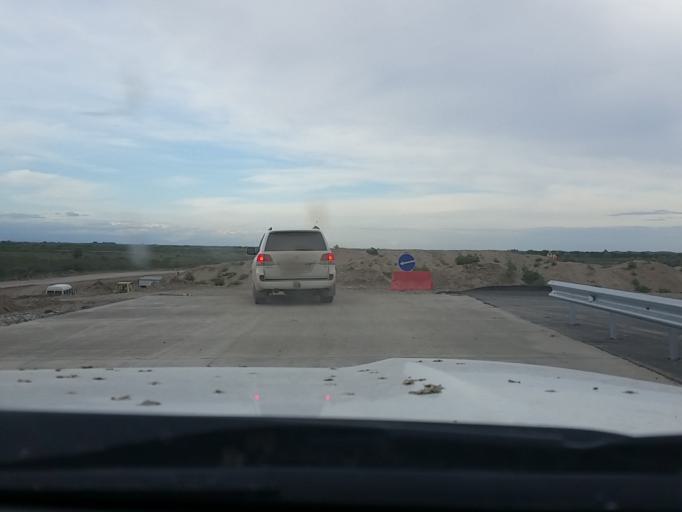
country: KZ
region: Almaty Oblysy
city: Zharkent
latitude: 44.1028
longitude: 80.0830
